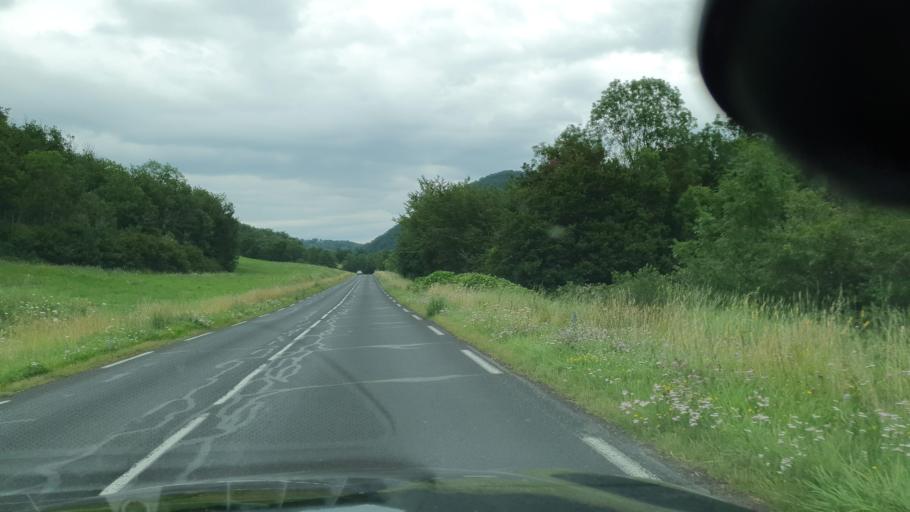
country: FR
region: Auvergne
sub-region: Departement du Puy-de-Dome
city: Champeix
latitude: 45.5737
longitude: 3.0298
